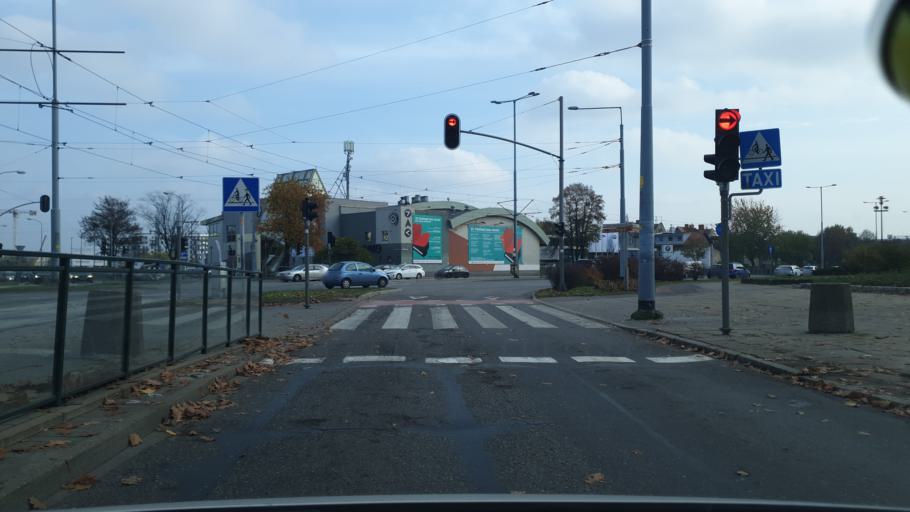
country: PL
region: Pomeranian Voivodeship
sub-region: Sopot
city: Sopot
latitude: 54.3870
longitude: 18.5907
